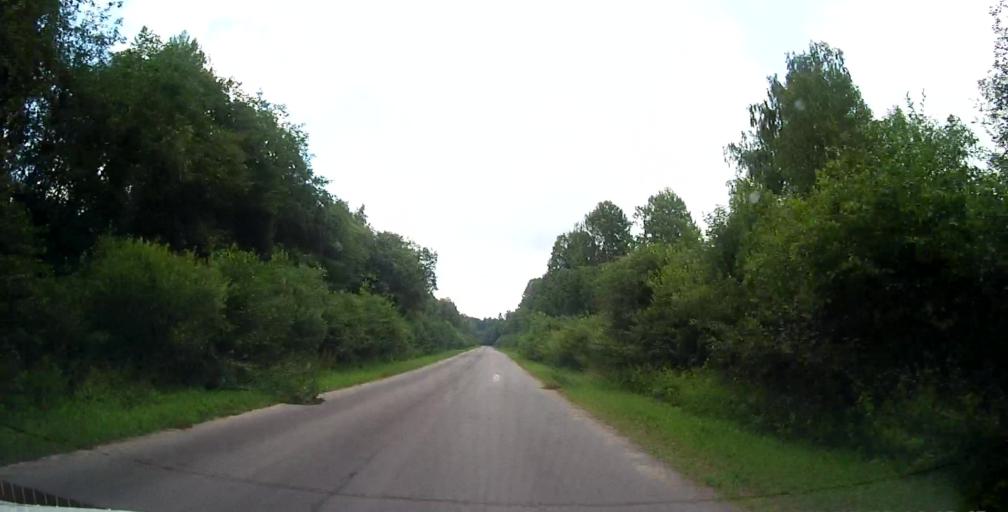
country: RU
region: Smolensk
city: Demidov
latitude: 55.4727
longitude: 31.6287
